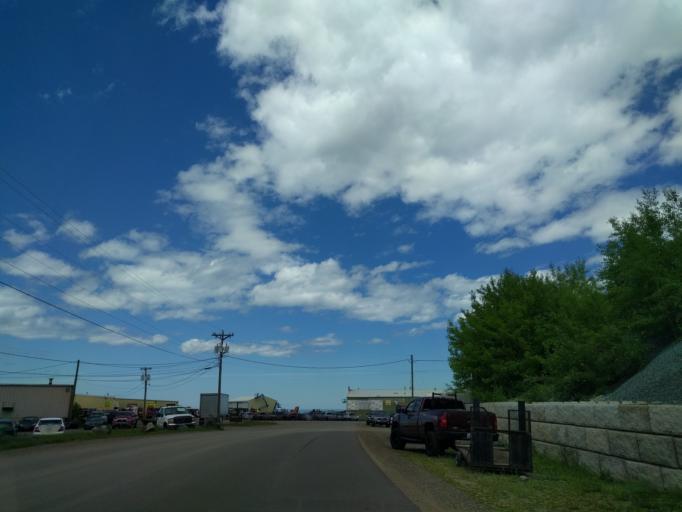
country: US
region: Michigan
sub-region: Marquette County
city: Trowbridge Park
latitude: 46.5395
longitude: -87.4987
